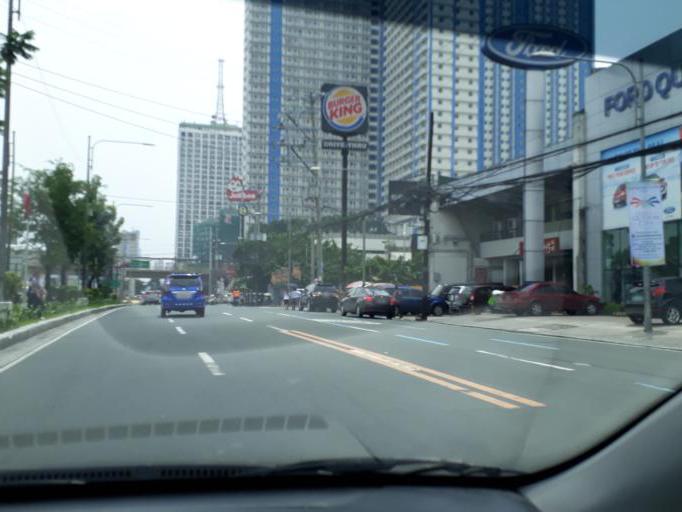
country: PH
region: Metro Manila
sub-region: City of Manila
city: Manila
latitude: 14.6189
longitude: 121.0029
